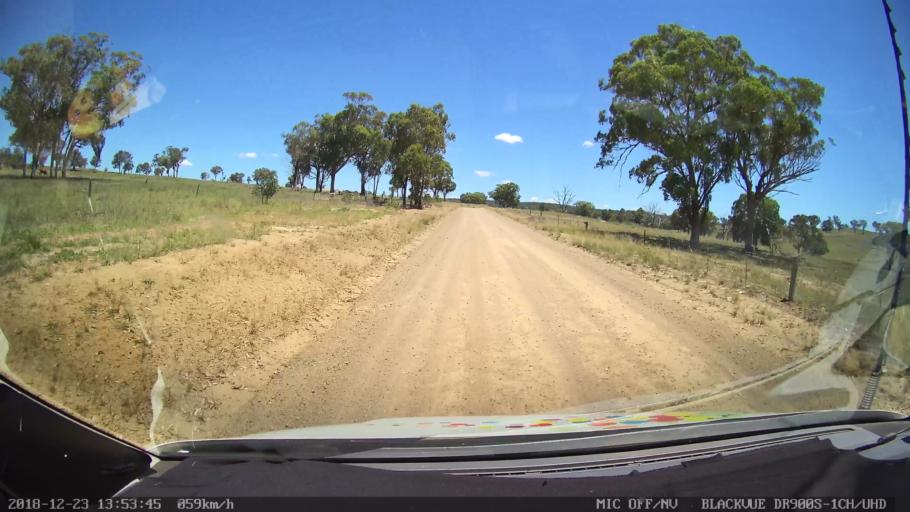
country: AU
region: New South Wales
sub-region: Tamworth Municipality
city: Manilla
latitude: -30.5549
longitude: 151.0925
